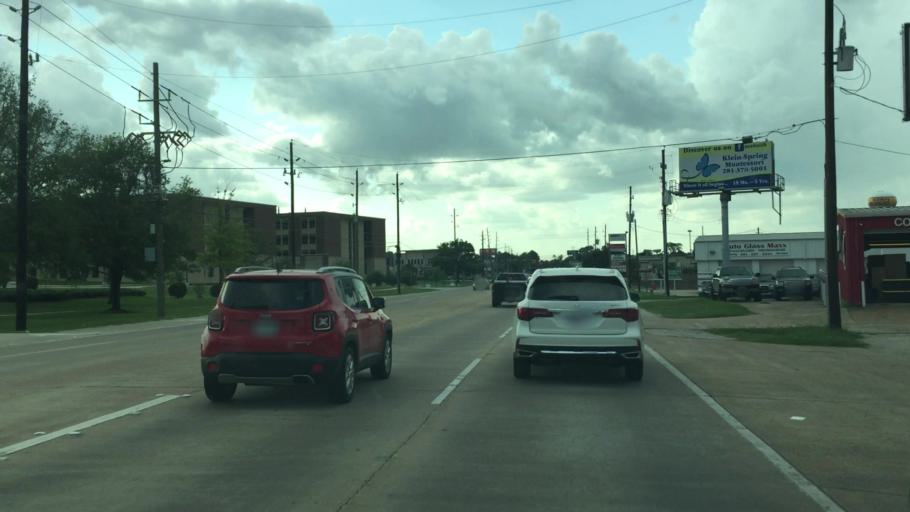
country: US
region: Texas
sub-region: Harris County
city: Hudson
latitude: 30.0192
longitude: -95.5215
